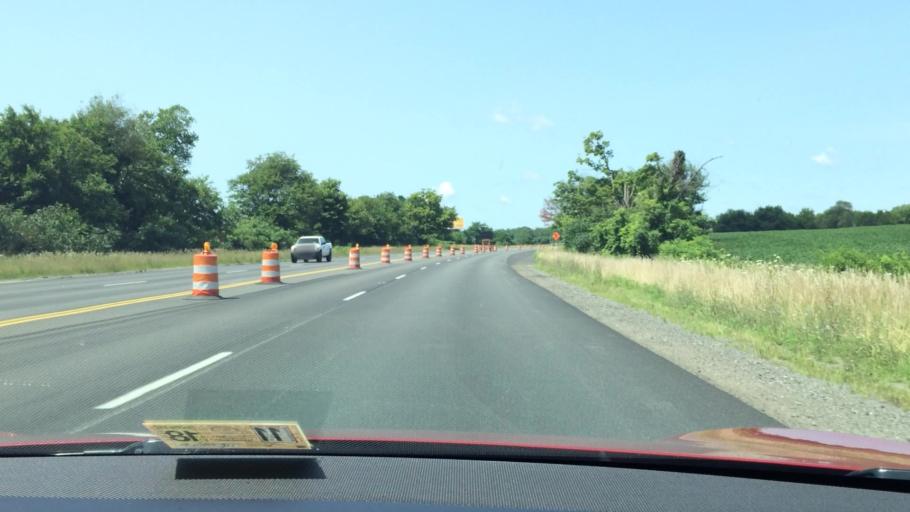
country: US
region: Indiana
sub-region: LaPorte County
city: Hudson Lake
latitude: 41.6699
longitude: -86.6087
